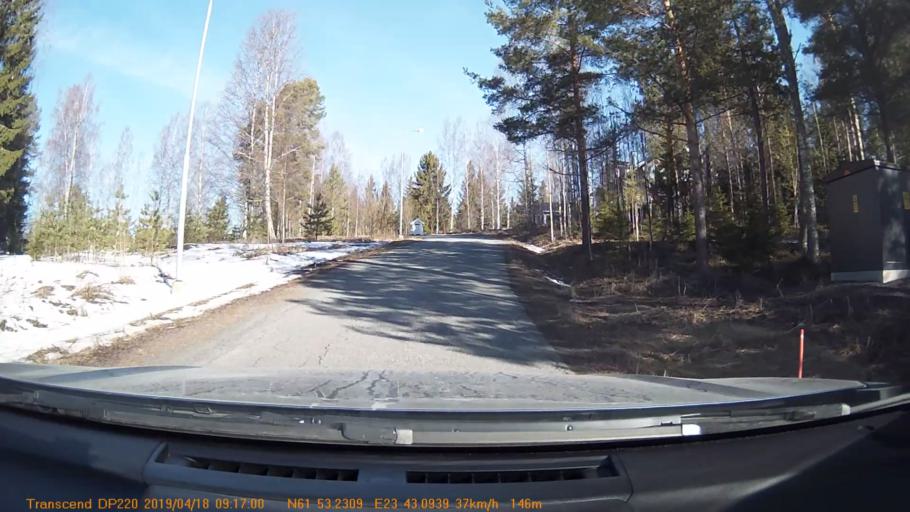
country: FI
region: Pirkanmaa
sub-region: Tampere
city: Kuru
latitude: 61.8878
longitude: 23.7168
